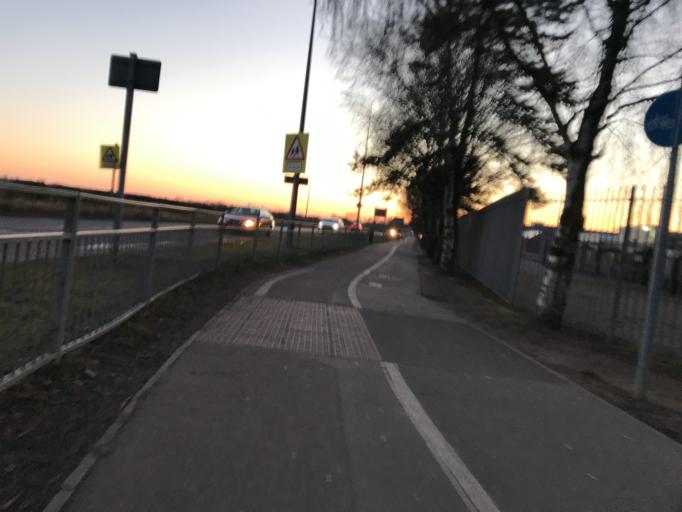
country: GB
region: England
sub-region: Lincolnshire
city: Holton le Clay
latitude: 53.5215
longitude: -0.0755
